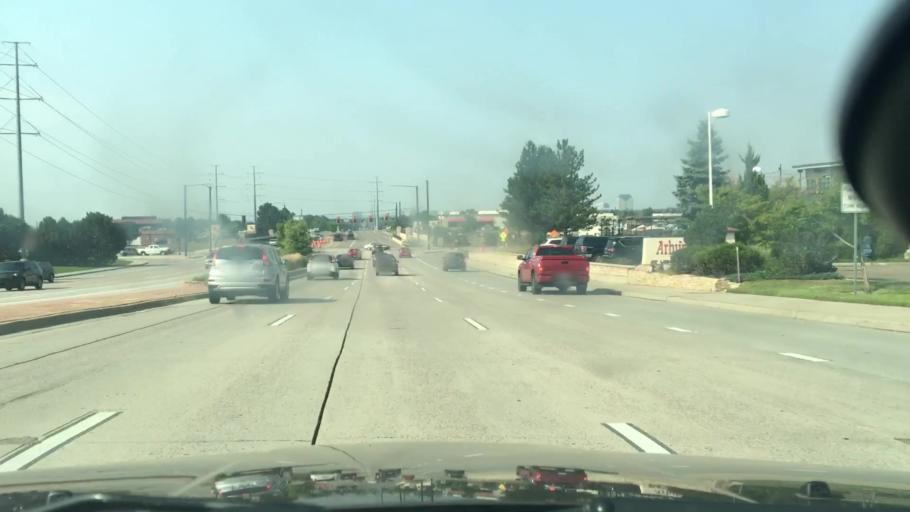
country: US
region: Colorado
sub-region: Douglas County
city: Acres Green
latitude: 39.5616
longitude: -104.9043
